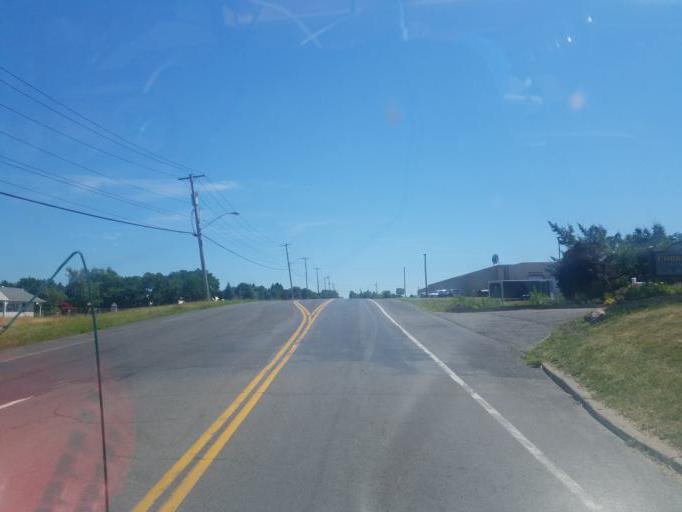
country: US
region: New York
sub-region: Ontario County
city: Geneva
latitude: 42.8563
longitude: -77.0107
